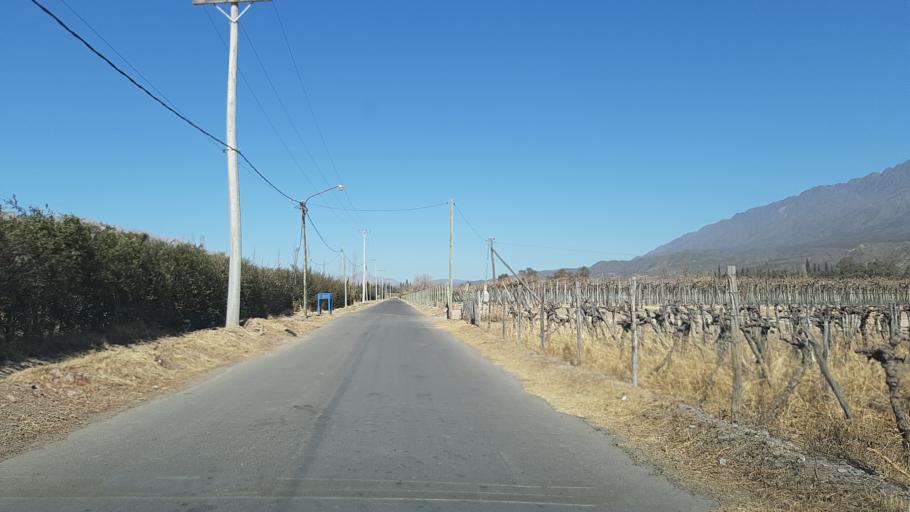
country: AR
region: San Juan
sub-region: Departamento de Zonda
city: Zonda
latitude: -31.5671
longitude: -68.7504
